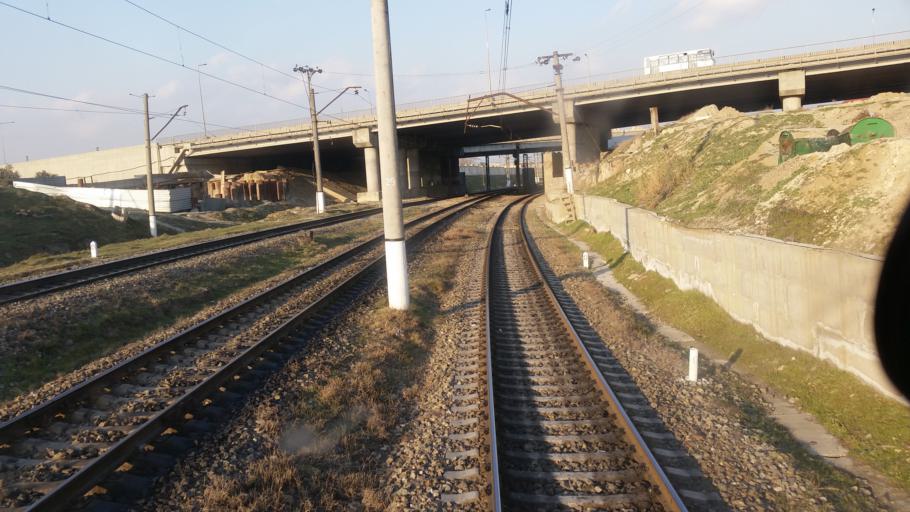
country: AZ
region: Baki
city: Bilajari
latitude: 40.4283
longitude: 49.7889
